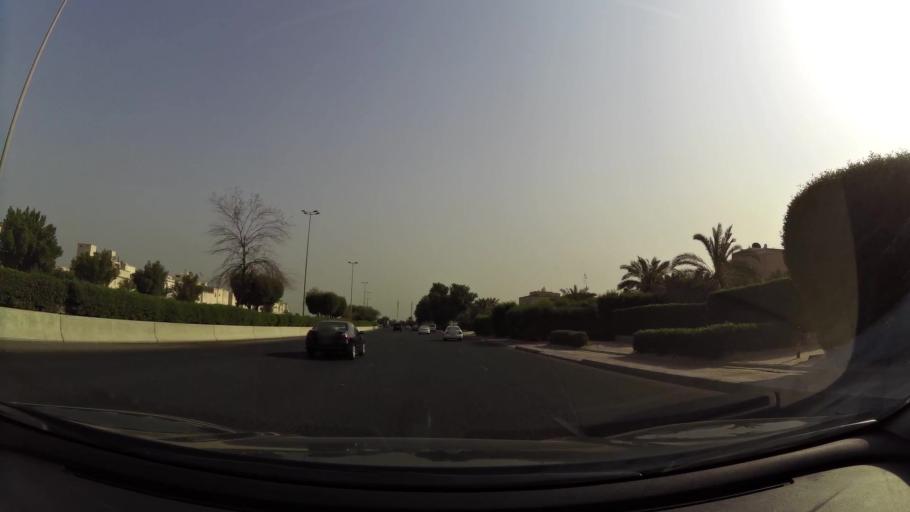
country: KW
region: Mubarak al Kabir
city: Sabah as Salim
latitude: 29.2337
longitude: 48.0726
